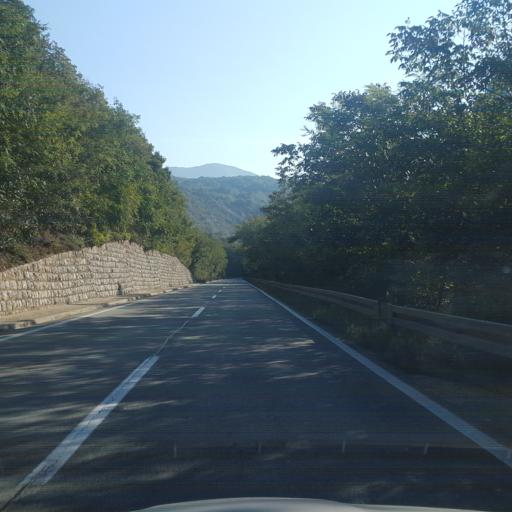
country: RS
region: Central Serbia
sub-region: Nisavski Okrug
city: Niska Banja
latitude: 43.3339
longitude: 22.0784
